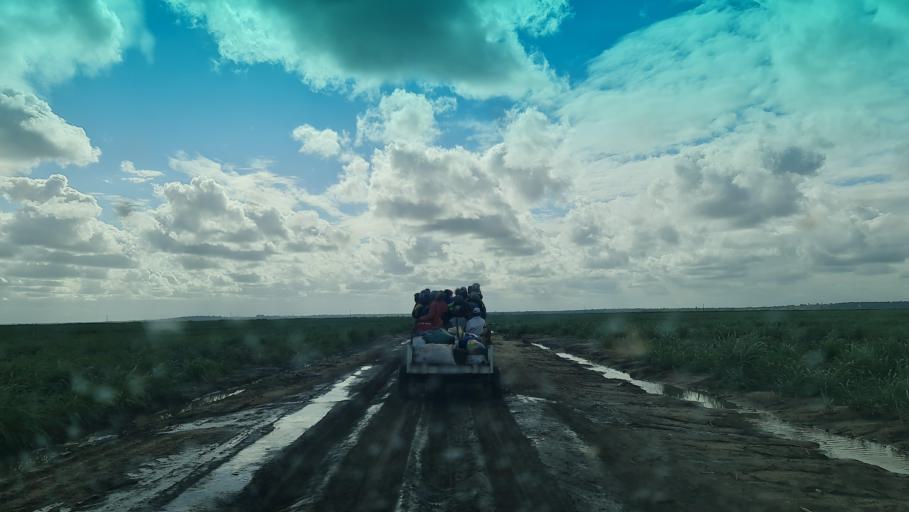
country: MZ
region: Maputo
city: Manhica
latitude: -25.4382
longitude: 32.8482
